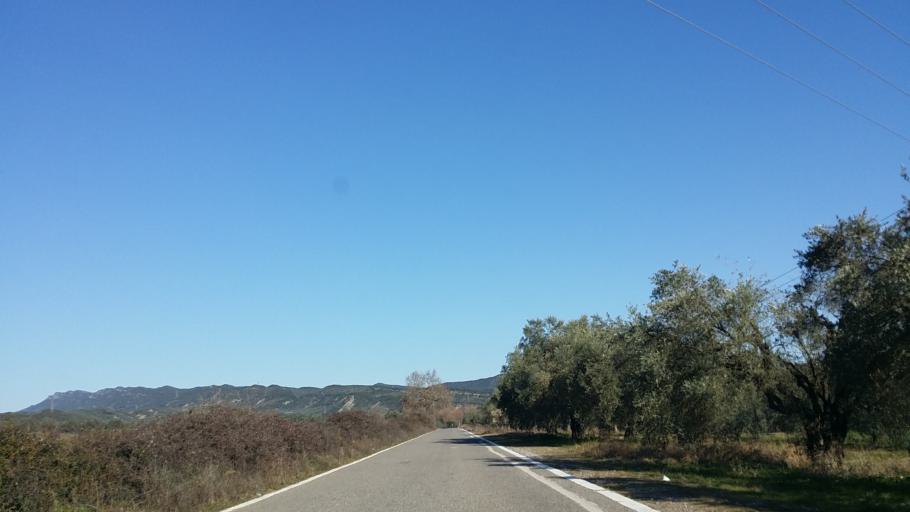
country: GR
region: West Greece
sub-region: Nomos Aitolias kai Akarnanias
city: Lepenou
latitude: 38.7249
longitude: 21.3333
